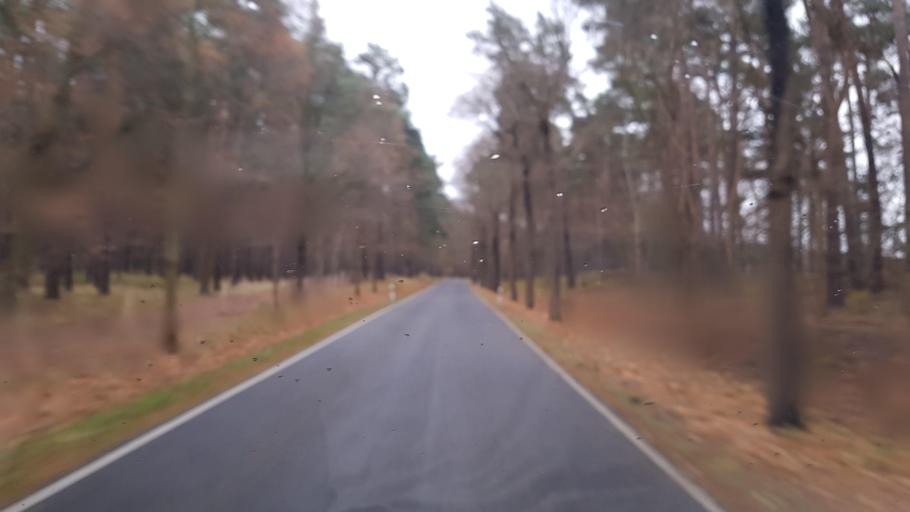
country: DE
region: Brandenburg
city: Tauche
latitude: 52.0990
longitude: 14.1639
